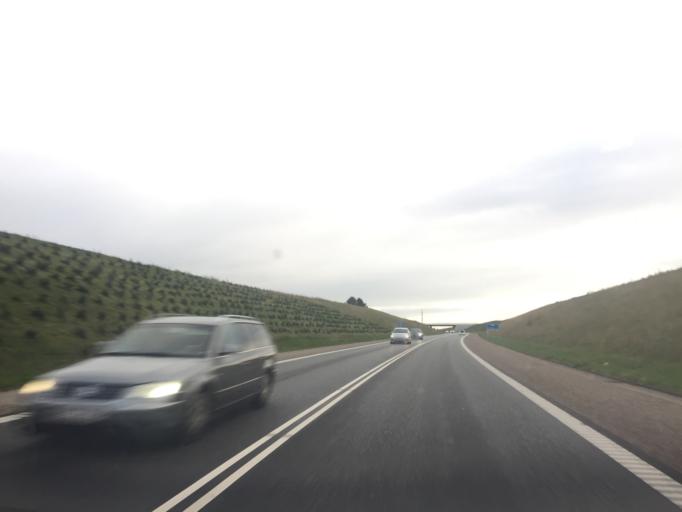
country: DK
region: Capital Region
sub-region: Egedal Kommune
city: Smorumnedre
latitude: 55.7361
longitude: 12.2838
